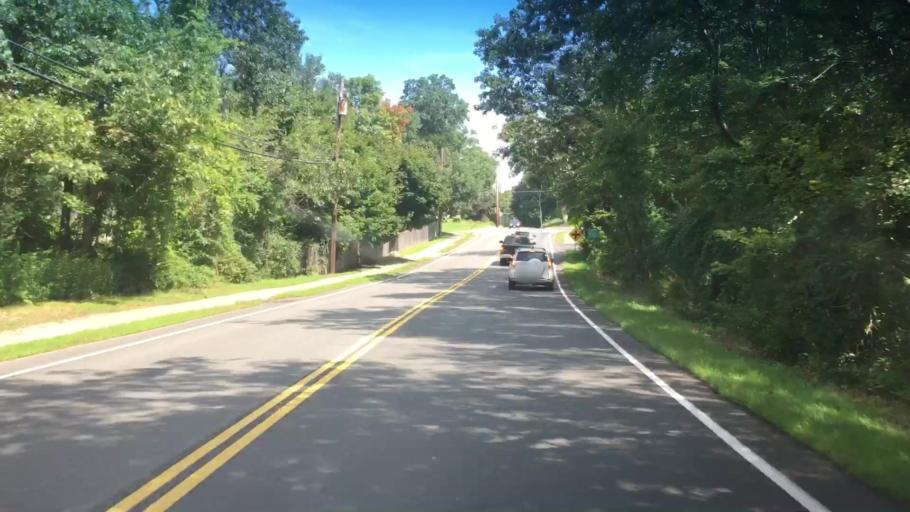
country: US
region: Massachusetts
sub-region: Norfolk County
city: Westwood
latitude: 42.2215
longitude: -71.2275
